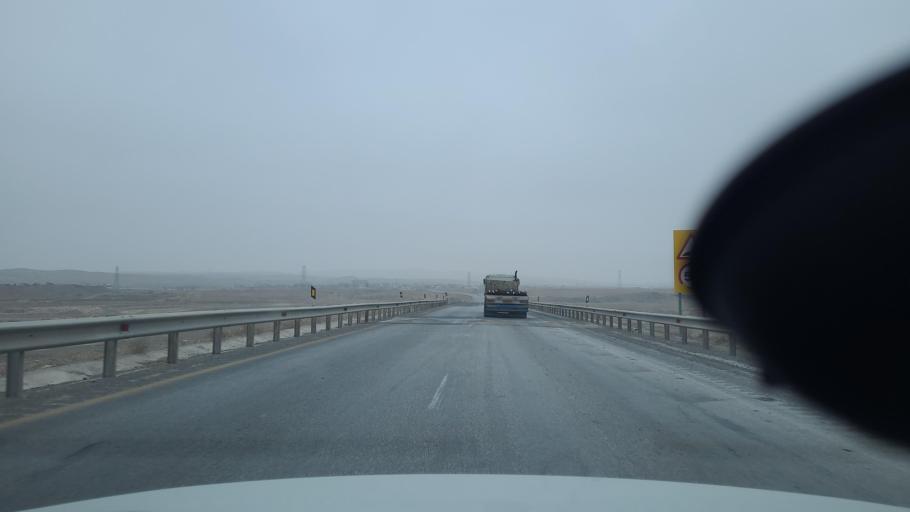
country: IR
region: Razavi Khorasan
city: Fariman
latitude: 35.9849
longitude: 59.7435
